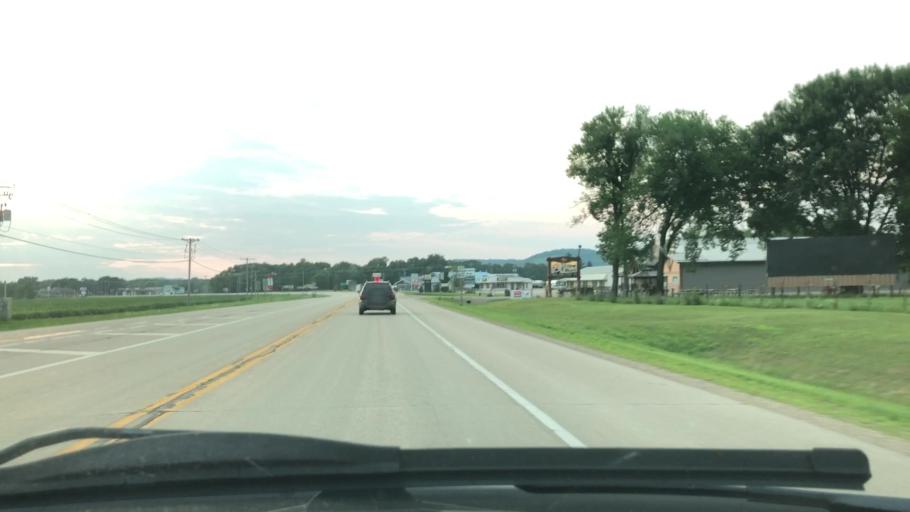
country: US
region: Wisconsin
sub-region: Sauk County
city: Spring Green
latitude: 43.1838
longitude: -90.0663
